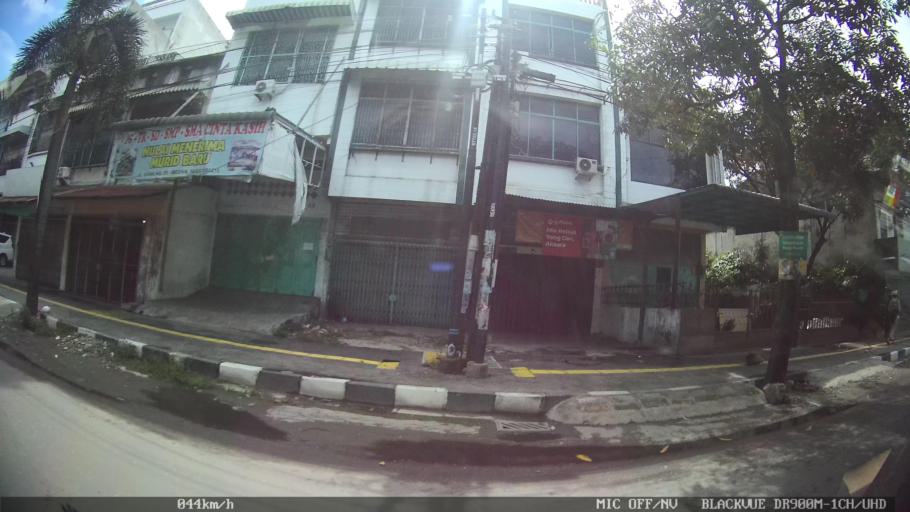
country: ID
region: North Sumatra
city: Medan
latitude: 3.5907
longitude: 98.7062
